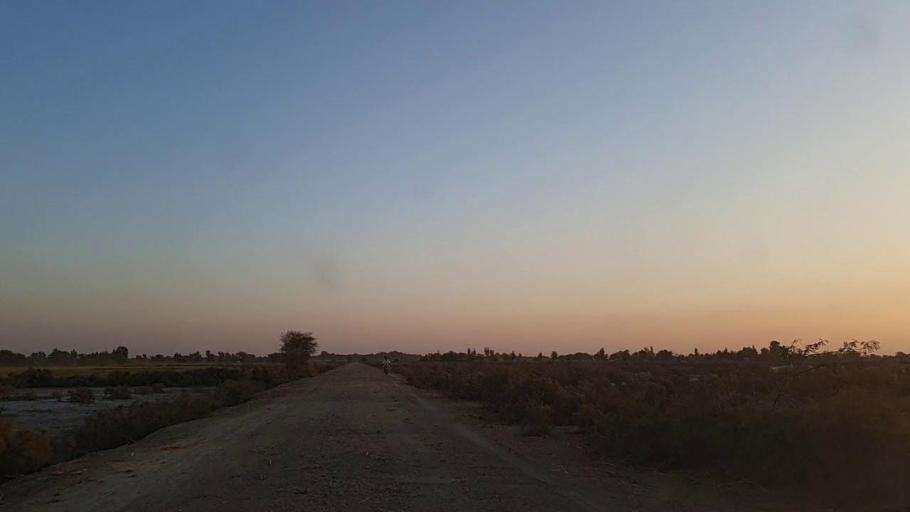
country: PK
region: Sindh
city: Samaro
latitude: 25.3174
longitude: 69.3692
